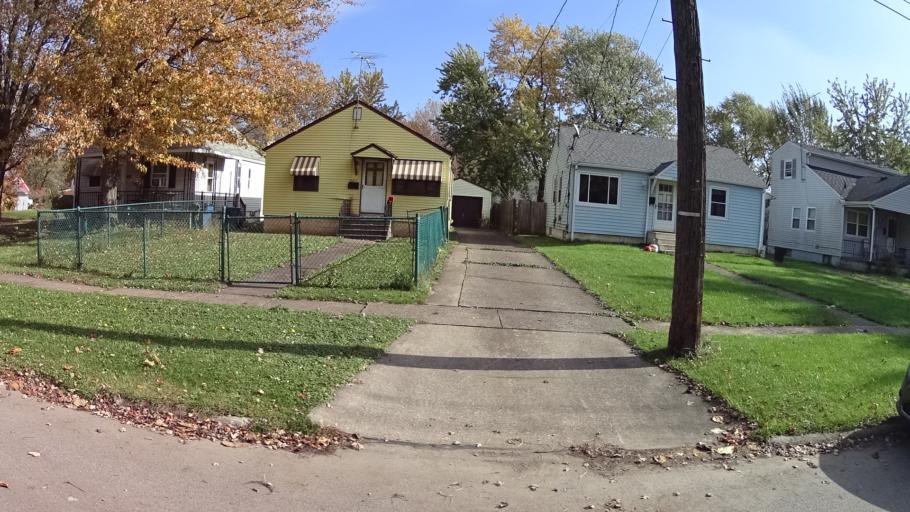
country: US
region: Ohio
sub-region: Lorain County
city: Lorain
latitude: 41.4668
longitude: -82.1411
